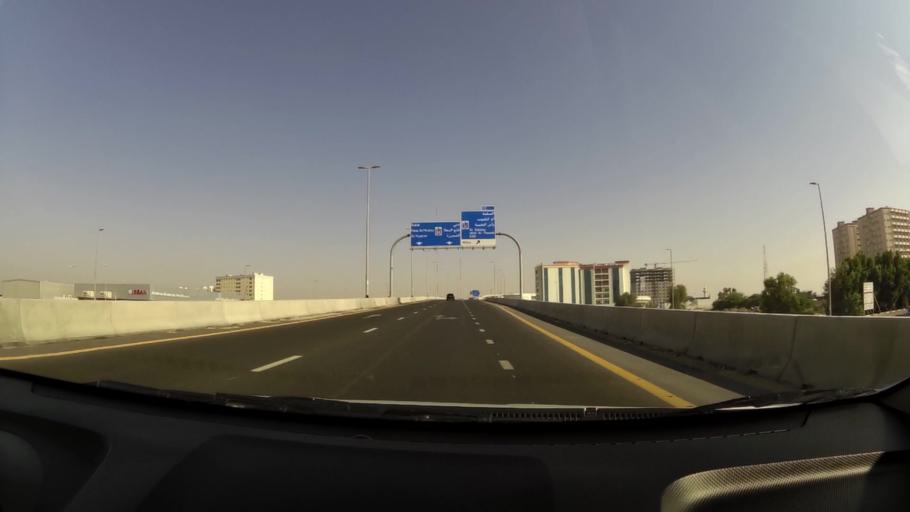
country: AE
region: Umm al Qaywayn
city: Umm al Qaywayn
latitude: 25.4970
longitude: 55.5519
